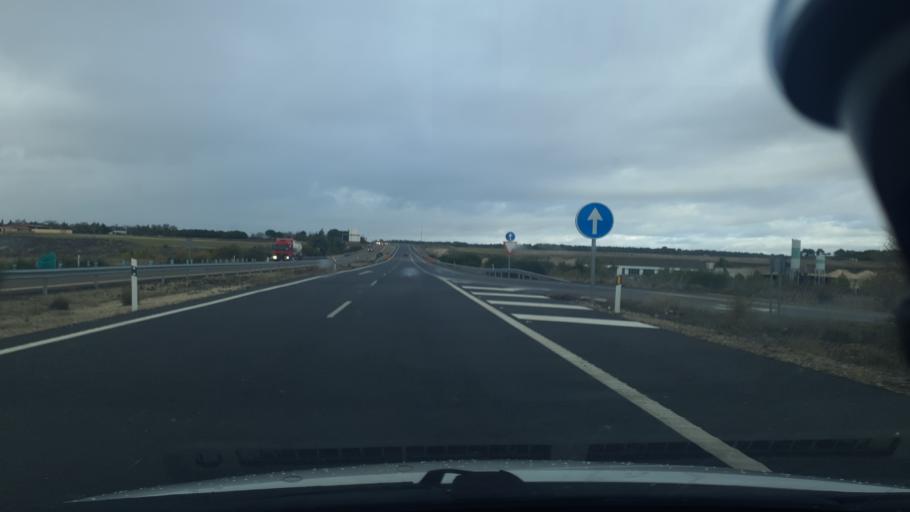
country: ES
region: Castille and Leon
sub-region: Provincia de Segovia
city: Cuellar
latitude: 41.4061
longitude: -4.2954
